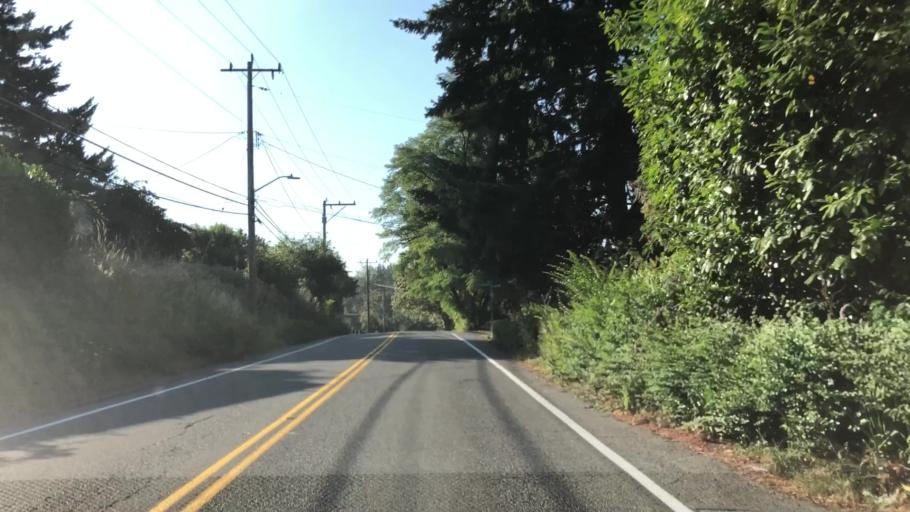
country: US
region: Washington
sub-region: King County
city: Tukwila
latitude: 47.4903
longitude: -122.2573
